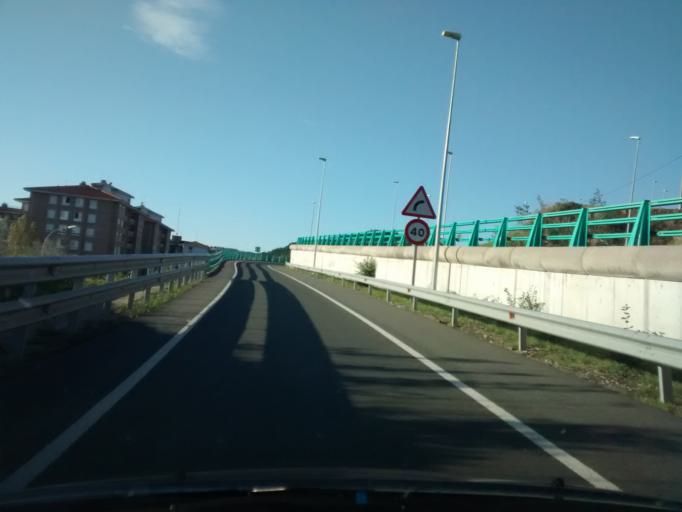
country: ES
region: Basque Country
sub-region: Bizkaia
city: Abadino
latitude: 43.1679
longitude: -2.6062
